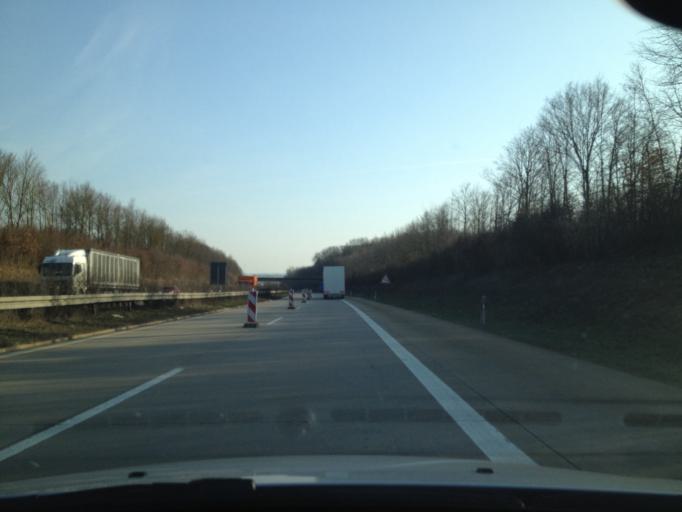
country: DE
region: Bavaria
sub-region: Regierungsbezirk Mittelfranken
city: Gollhofen
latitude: 49.5822
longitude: 10.1715
